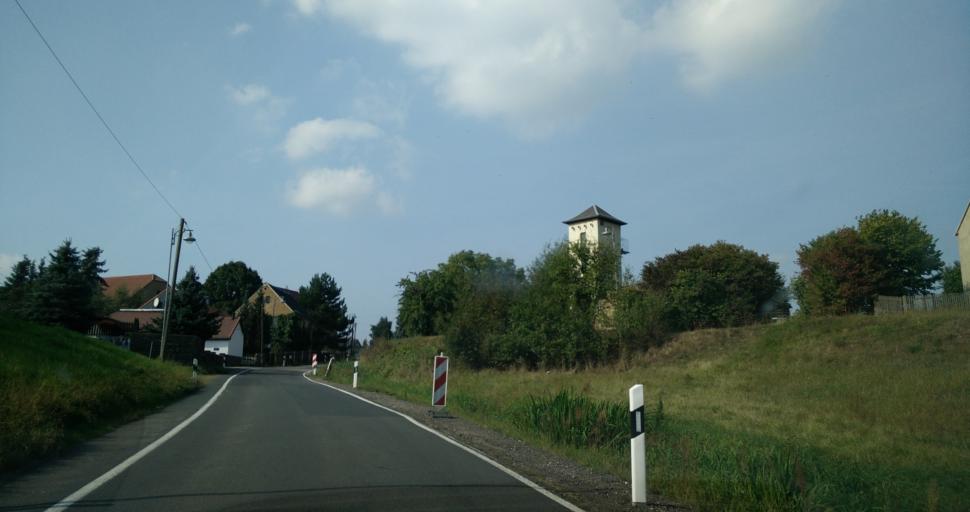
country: DE
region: Saxony
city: Colditz
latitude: 51.1112
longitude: 12.8056
